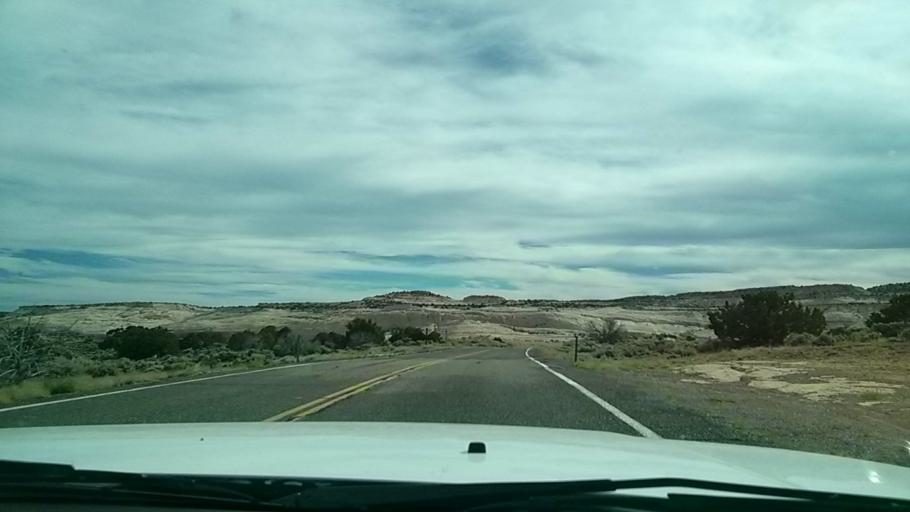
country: US
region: Utah
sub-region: Wayne County
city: Loa
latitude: 37.7542
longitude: -111.4364
